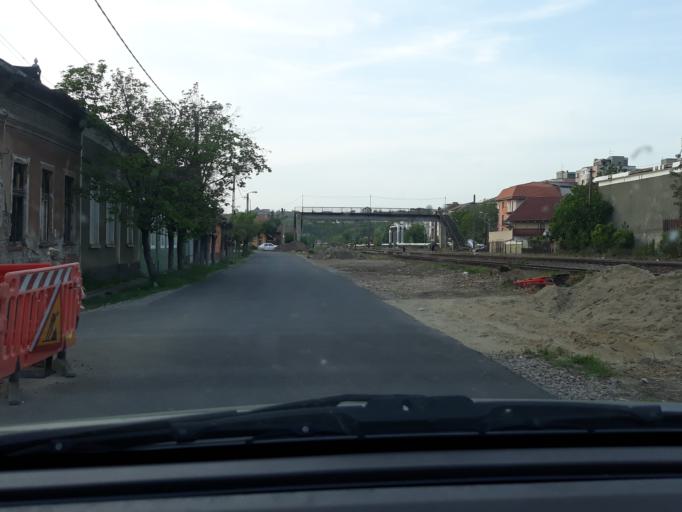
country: RO
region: Bihor
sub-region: Comuna Biharea
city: Oradea
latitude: 47.0460
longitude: 21.9609
